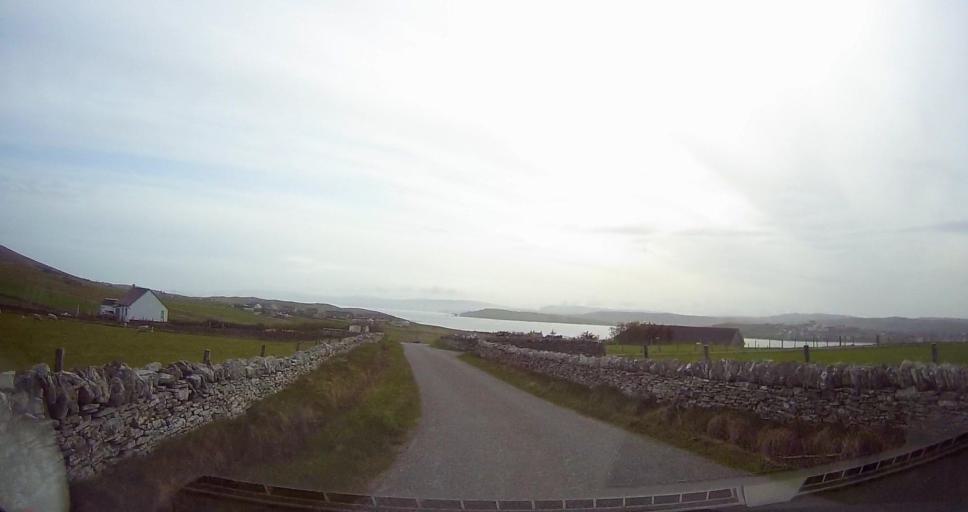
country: GB
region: Scotland
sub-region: Shetland Islands
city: Shetland
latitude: 60.1512
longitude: -1.1026
